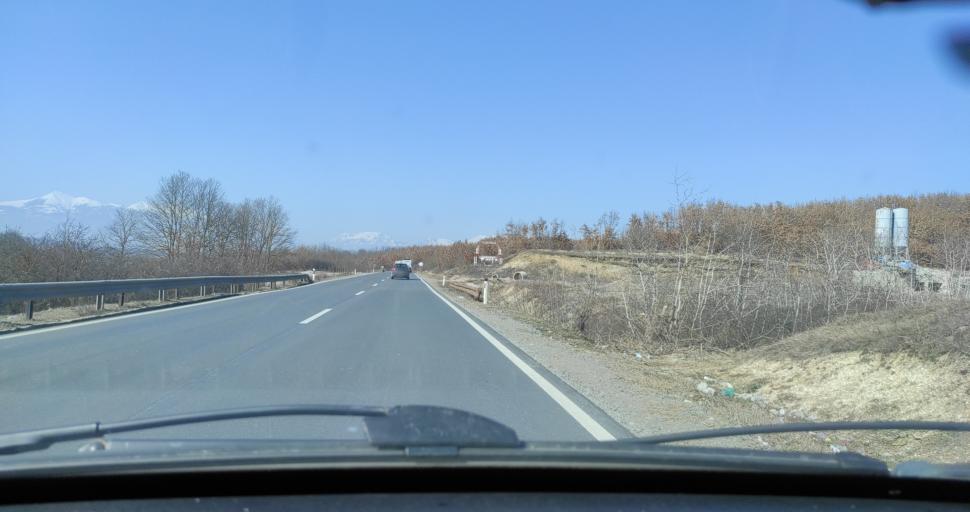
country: XK
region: Pec
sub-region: Komuna e Klines
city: Klina
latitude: 42.5949
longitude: 20.5409
